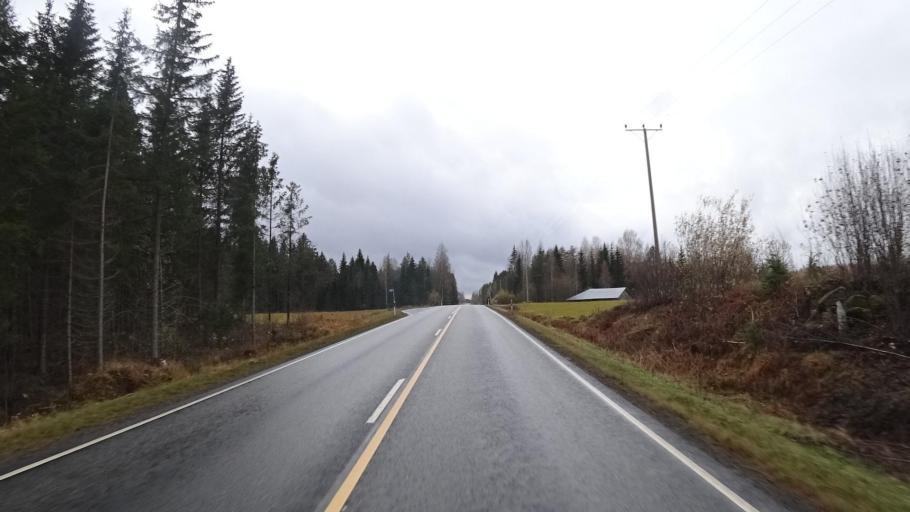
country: FI
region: Southern Savonia
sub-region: Pieksaemaeki
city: Pieksaemaeki
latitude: 62.1790
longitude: 26.8708
